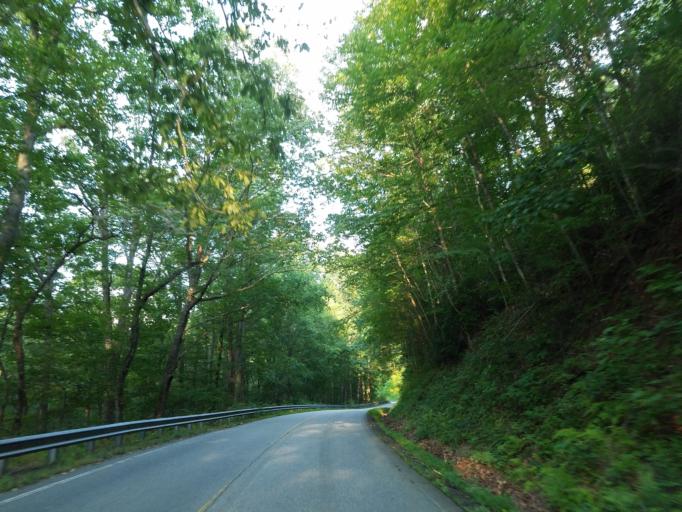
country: US
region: Georgia
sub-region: Lumpkin County
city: Dahlonega
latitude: 34.7013
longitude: -84.0373
